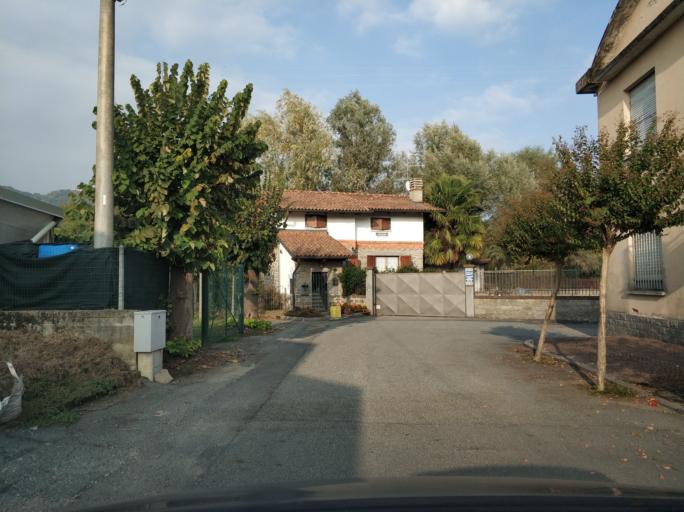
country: IT
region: Piedmont
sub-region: Provincia di Biella
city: Ronco Biellese
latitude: 45.5678
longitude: 8.0875
